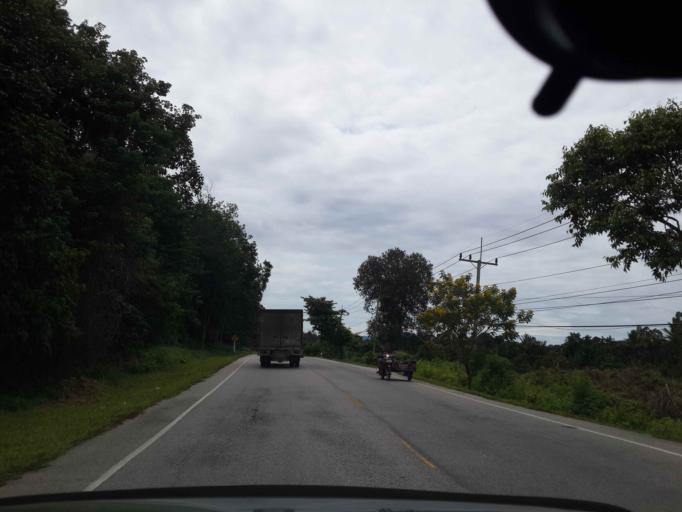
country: TH
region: Narathiwat
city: Yi-ngo
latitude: 6.3544
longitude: 101.6160
